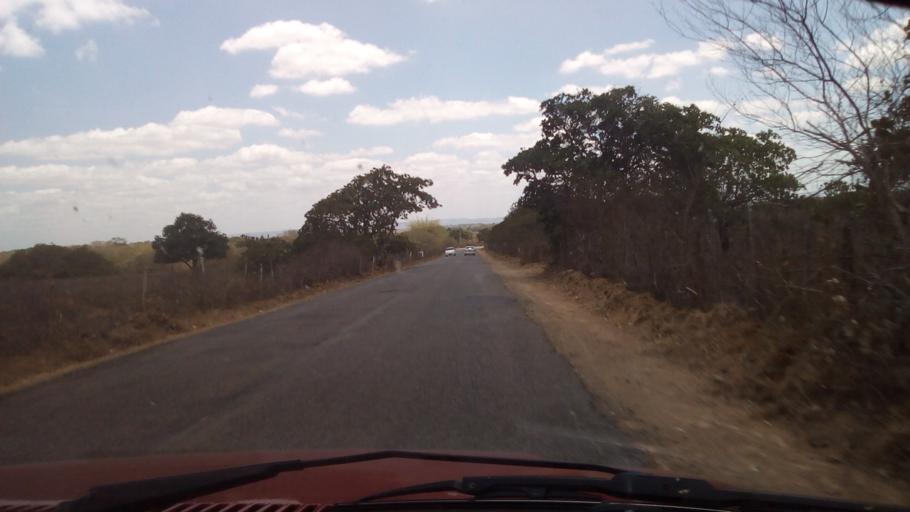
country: BR
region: Paraiba
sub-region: Cacimba De Dentro
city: Cacimba de Dentro
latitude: -6.5897
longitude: -35.8161
